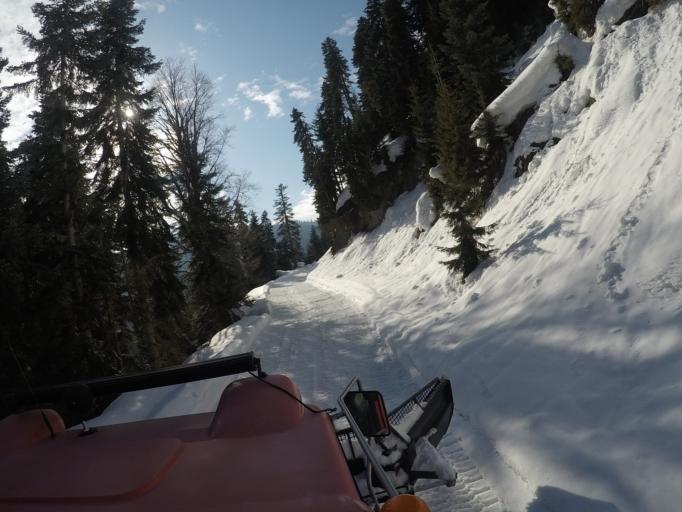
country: GE
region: Samtskhe-Javakheti
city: Adigeni
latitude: 41.6439
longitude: 42.5927
